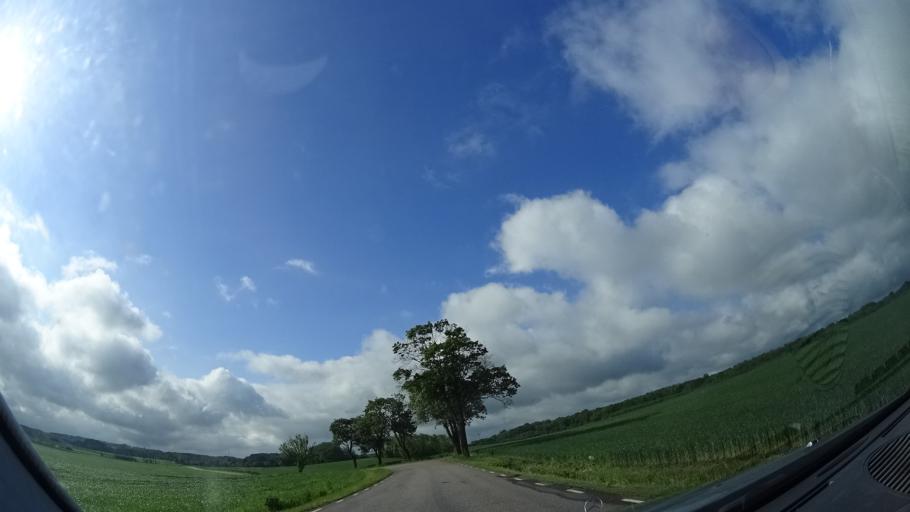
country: SE
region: Skane
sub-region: Eslovs Kommun
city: Stehag
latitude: 55.9118
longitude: 13.3898
